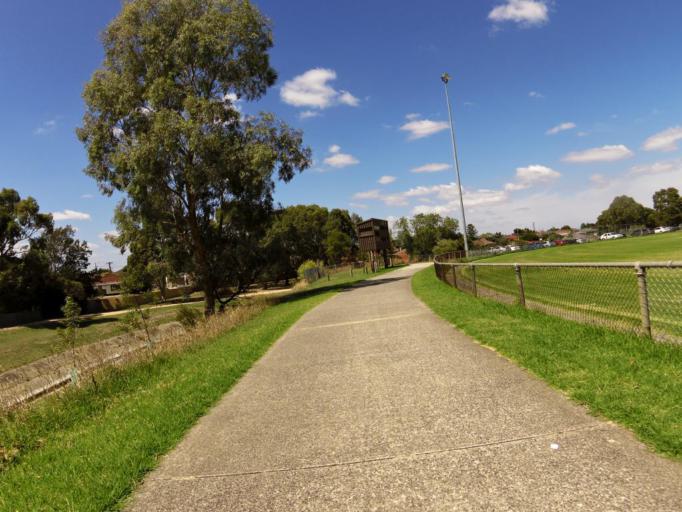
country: AU
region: Victoria
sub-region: Whittlesea
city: Thomastown
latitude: -37.6774
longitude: 145.0073
